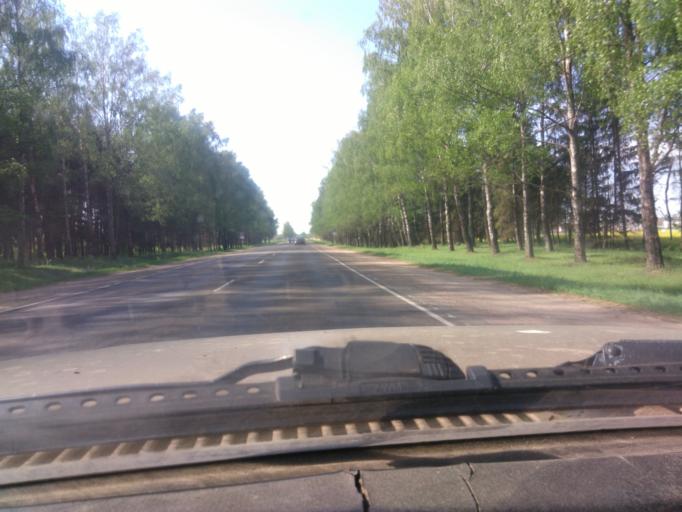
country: BY
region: Mogilev
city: Buynichy
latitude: 53.8440
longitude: 30.2500
